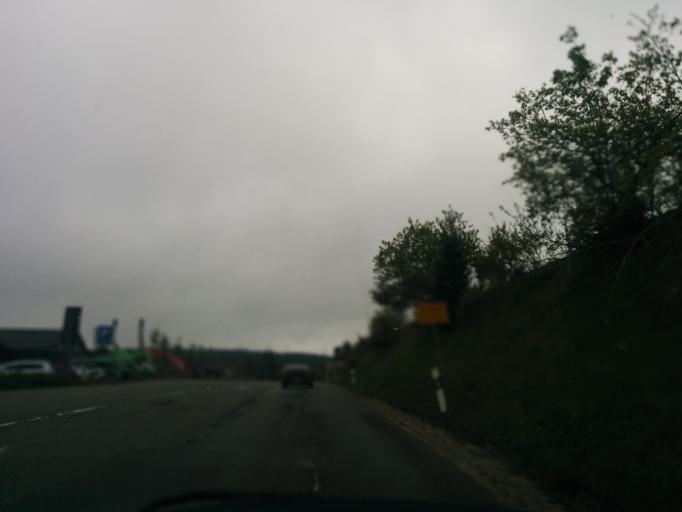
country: DE
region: Lower Saxony
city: Bad Harzburg
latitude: 51.8035
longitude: 10.5358
